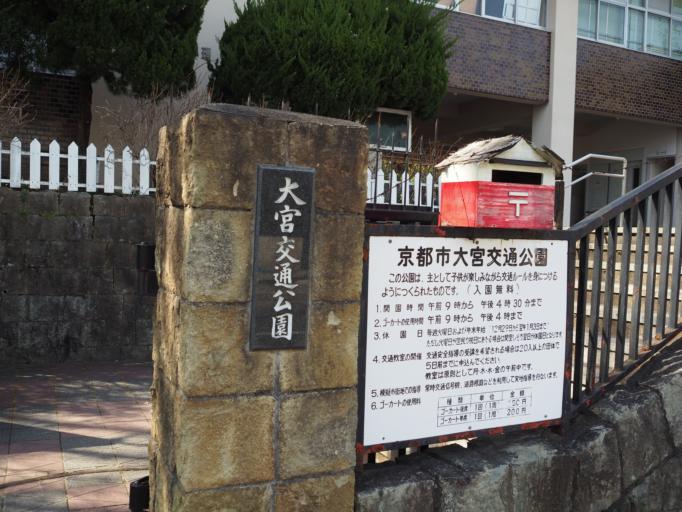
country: JP
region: Kyoto
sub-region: Kyoto-shi
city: Kamigyo-ku
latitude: 35.0534
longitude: 135.7440
